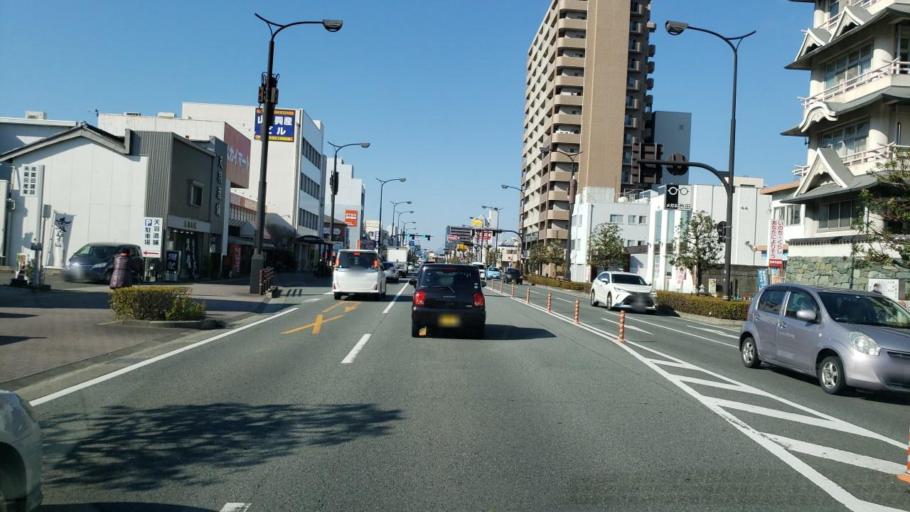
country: JP
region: Tokushima
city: Tokushima-shi
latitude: 34.0781
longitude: 134.5356
